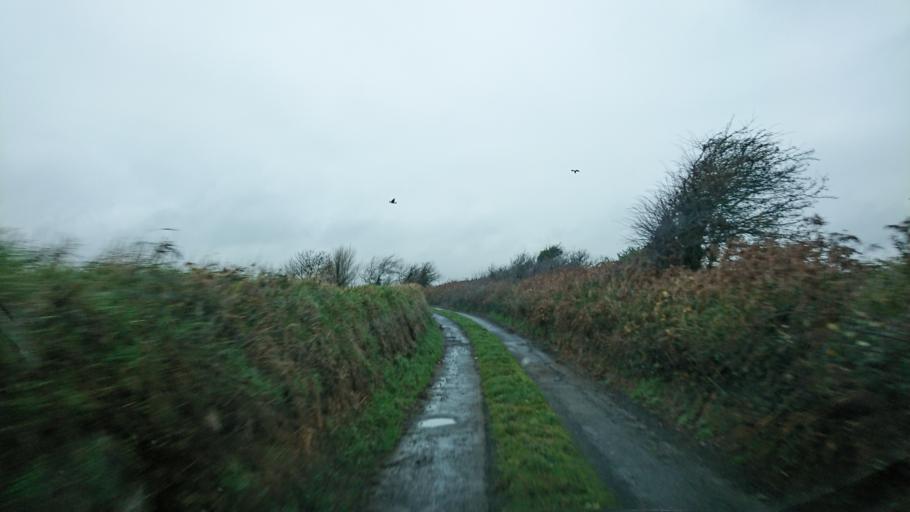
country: IE
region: Munster
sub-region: Waterford
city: Tra Mhor
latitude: 52.1993
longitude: -7.1516
